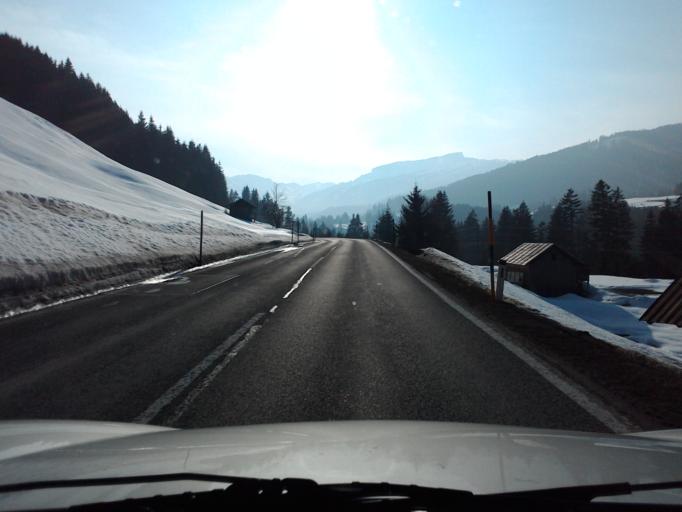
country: DE
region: Bavaria
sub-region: Swabia
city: Oberstdorf
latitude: 47.3759
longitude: 10.2121
